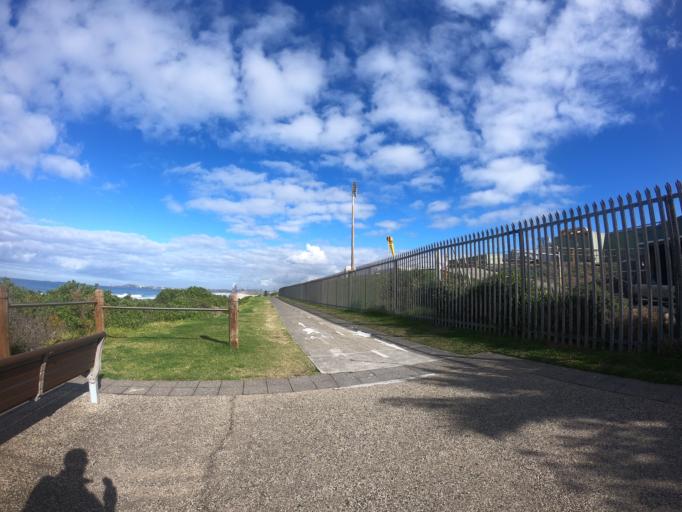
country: AU
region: New South Wales
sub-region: Wollongong
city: Wollongong
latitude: -34.4278
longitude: 150.9037
